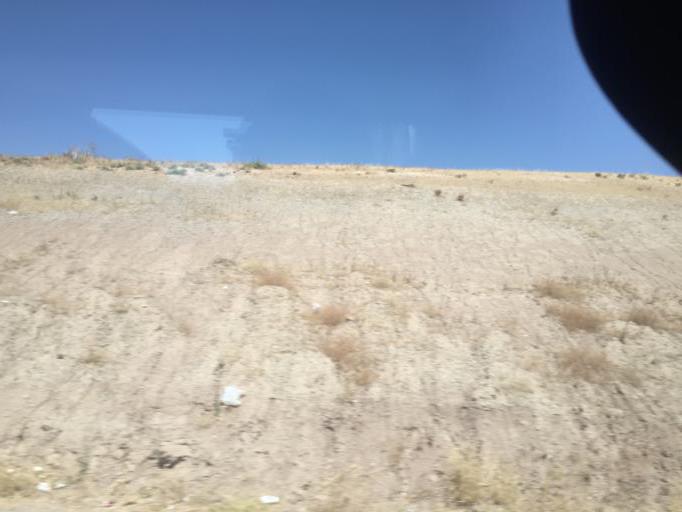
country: TR
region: Diyarbakir
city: Salat
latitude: 37.8604
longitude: 40.8687
